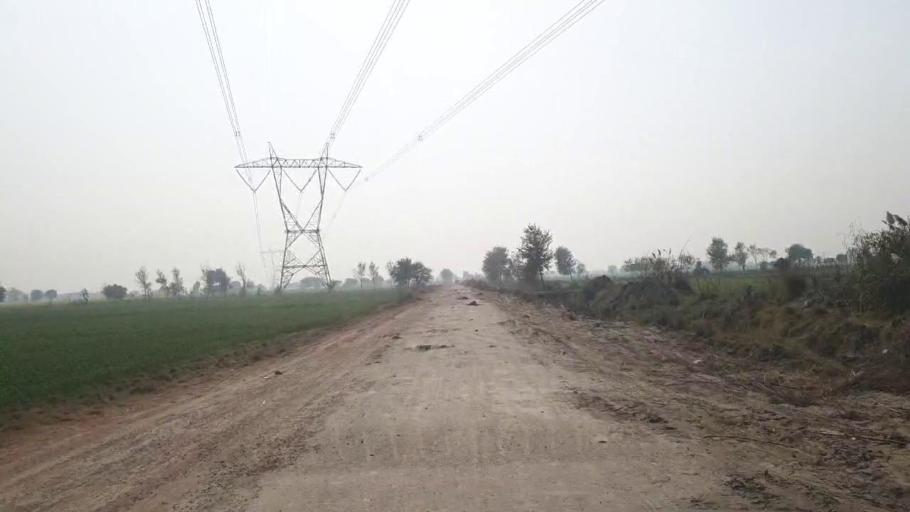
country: PK
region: Sindh
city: Hala
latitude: 25.9384
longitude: 68.4479
